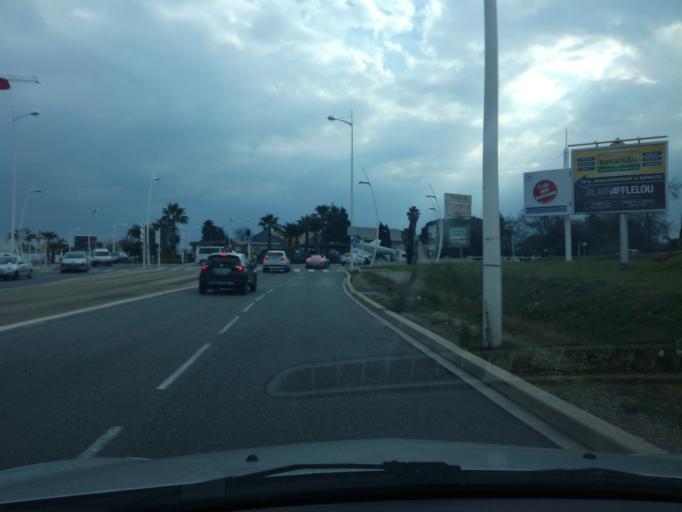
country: FR
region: Provence-Alpes-Cote d'Azur
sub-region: Departement des Alpes-Maritimes
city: Mandelieu-la-Napoule
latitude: 43.5508
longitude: 6.9565
